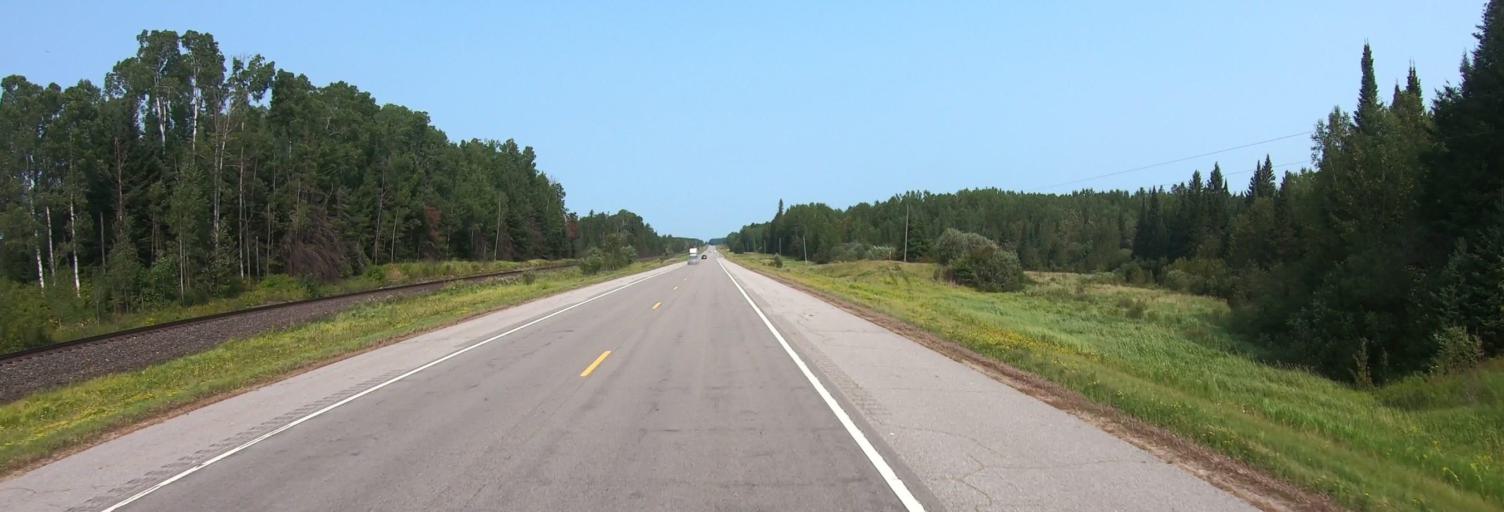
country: US
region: Minnesota
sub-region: Saint Louis County
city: Chisholm
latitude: 48.1559
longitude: -92.8698
